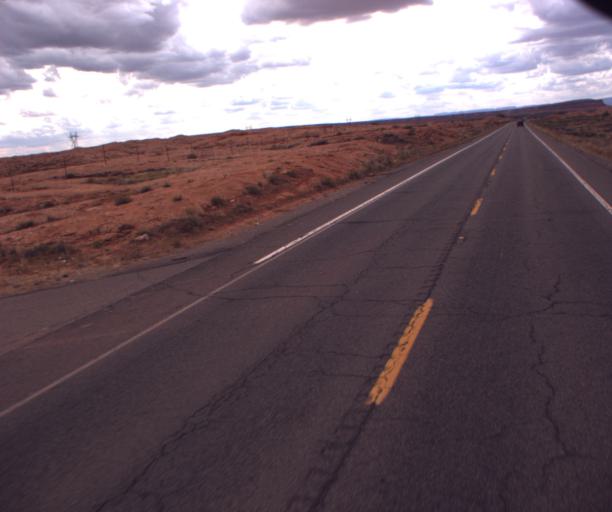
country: US
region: Arizona
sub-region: Navajo County
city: Kayenta
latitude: 36.8267
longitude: -109.8645
